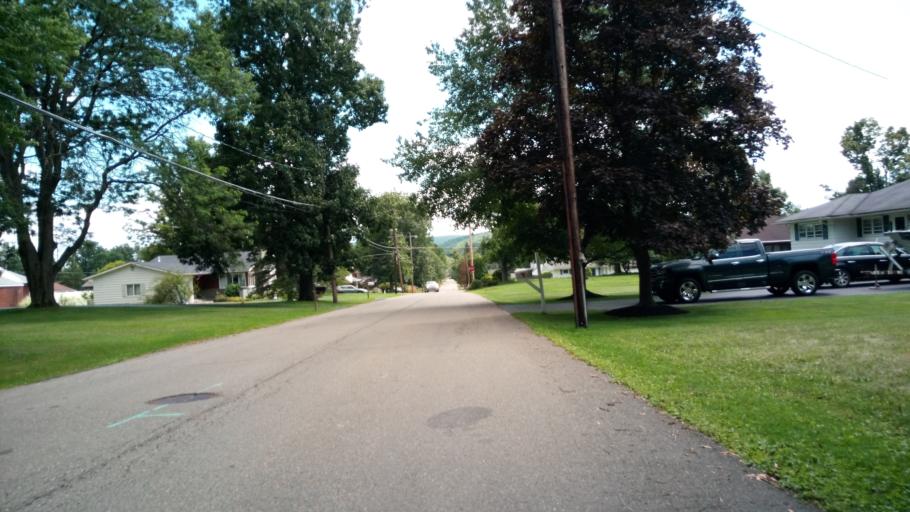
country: US
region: New York
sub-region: Chemung County
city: West Elmira
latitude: 42.0876
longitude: -76.8349
